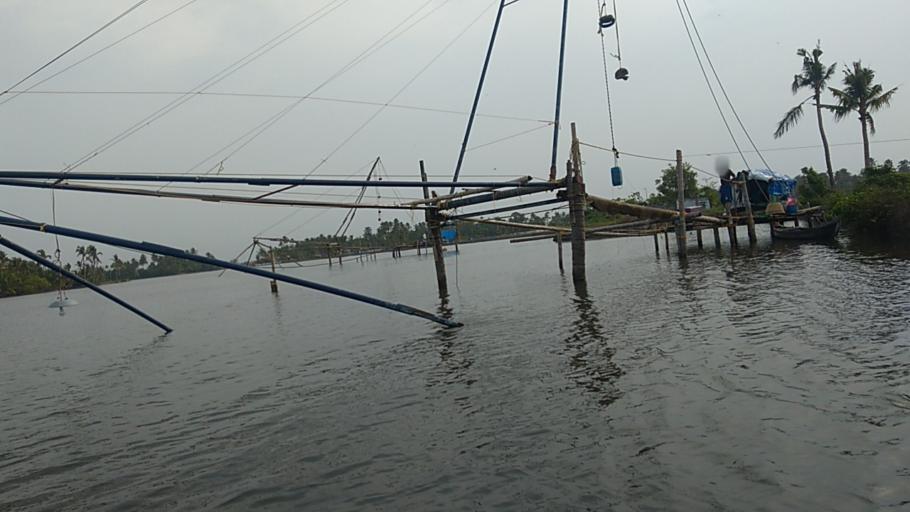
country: IN
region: Kerala
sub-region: Ernakulam
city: Elur
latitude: 10.0576
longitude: 76.2535
